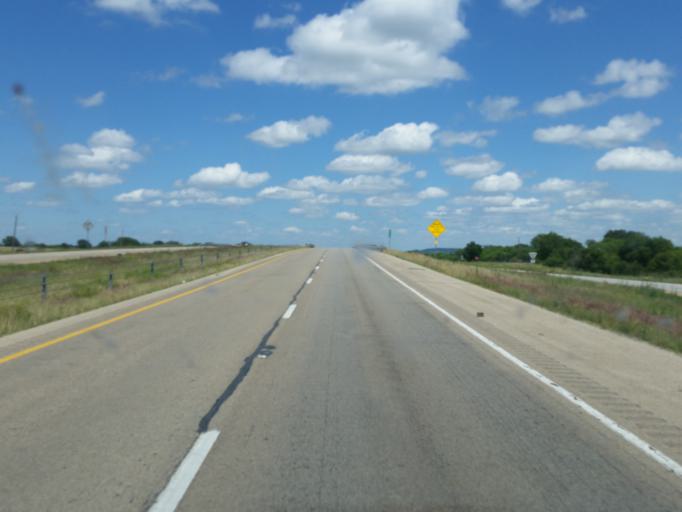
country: US
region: Texas
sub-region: Callahan County
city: Baird
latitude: 32.3861
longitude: -99.3011
